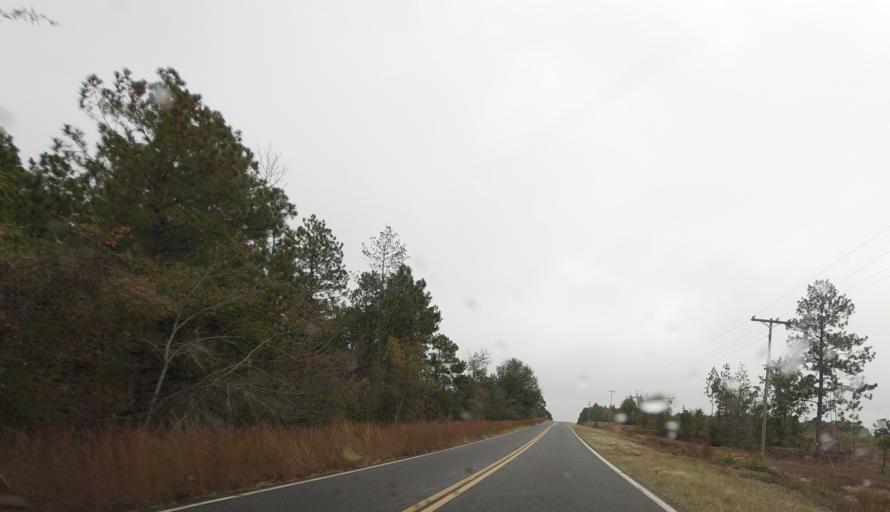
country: US
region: Georgia
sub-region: Taylor County
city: Butler
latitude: 32.4392
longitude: -84.3627
